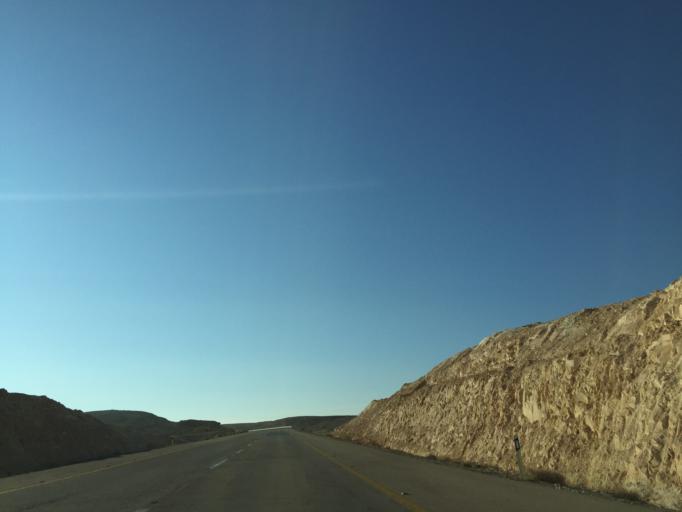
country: IL
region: Southern District
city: Mitzpe Ramon
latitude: 30.3144
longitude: 34.9671
